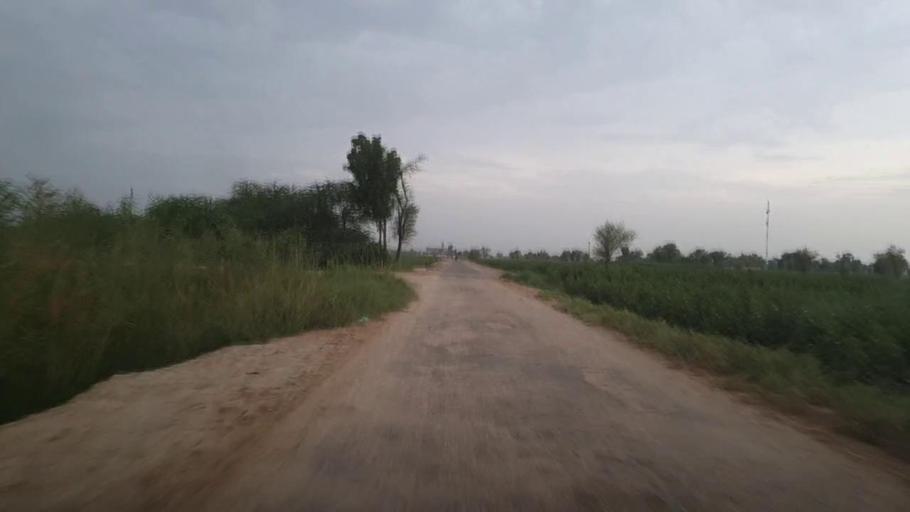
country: PK
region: Sindh
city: Karaundi
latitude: 27.0045
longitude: 68.3434
